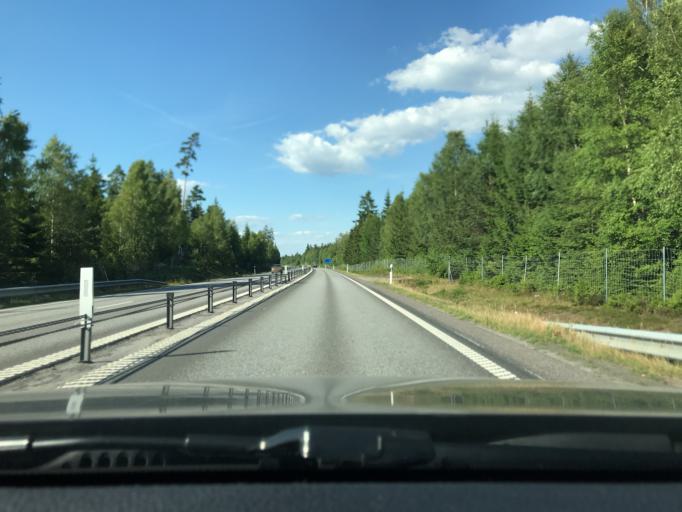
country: SE
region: Kronoberg
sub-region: Almhults Kommun
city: AElmhult
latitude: 56.4675
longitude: 14.1034
